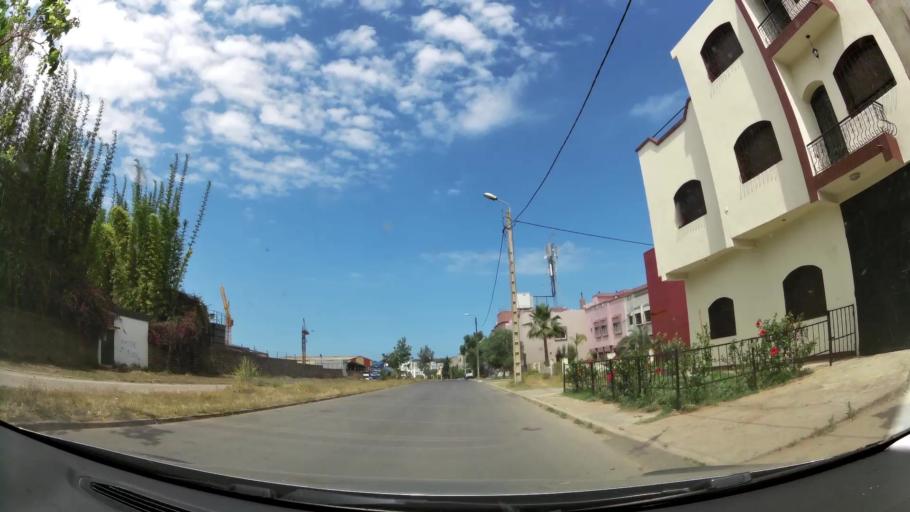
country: MA
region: Gharb-Chrarda-Beni Hssen
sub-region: Kenitra Province
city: Kenitra
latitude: 34.2416
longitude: -6.6102
